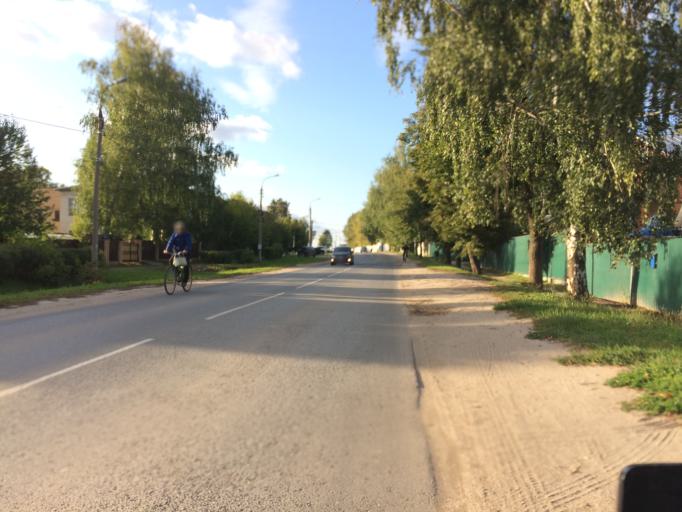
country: RU
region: Mariy-El
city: Yoshkar-Ola
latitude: 56.6522
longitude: 47.9791
